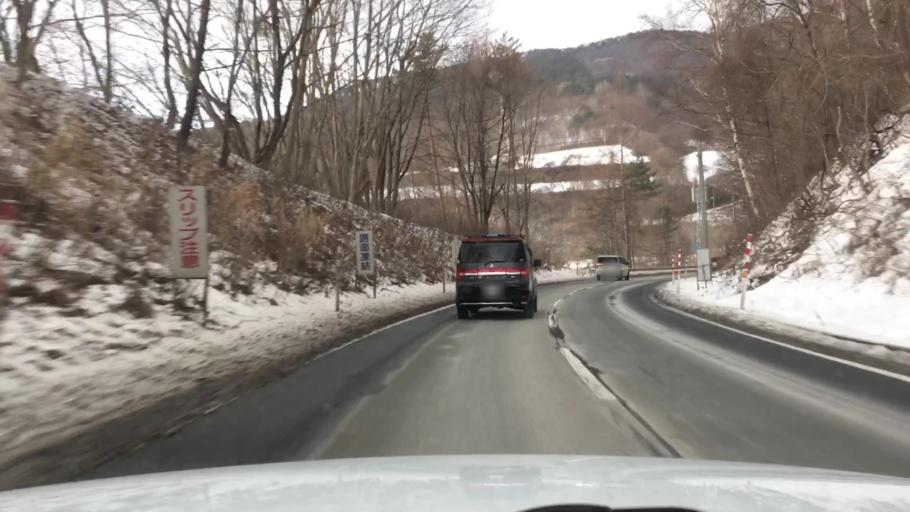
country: JP
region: Iwate
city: Morioka-shi
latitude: 39.6687
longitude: 141.3323
